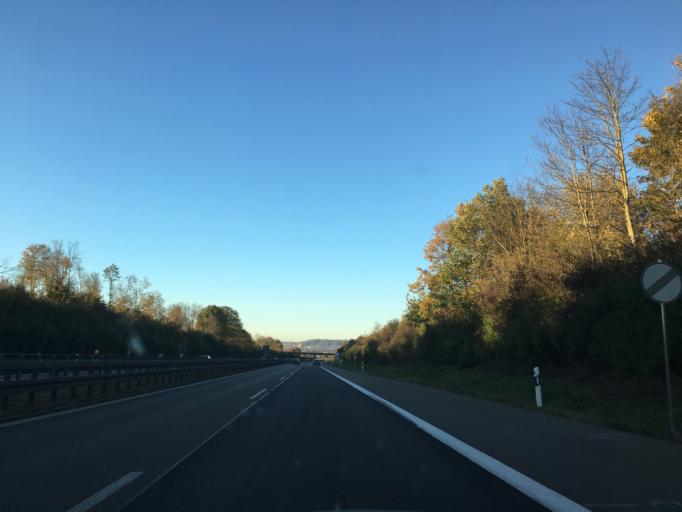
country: DE
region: Baden-Wuerttemberg
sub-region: Regierungsbezirk Stuttgart
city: Bondorf
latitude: 48.5422
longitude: 8.8905
